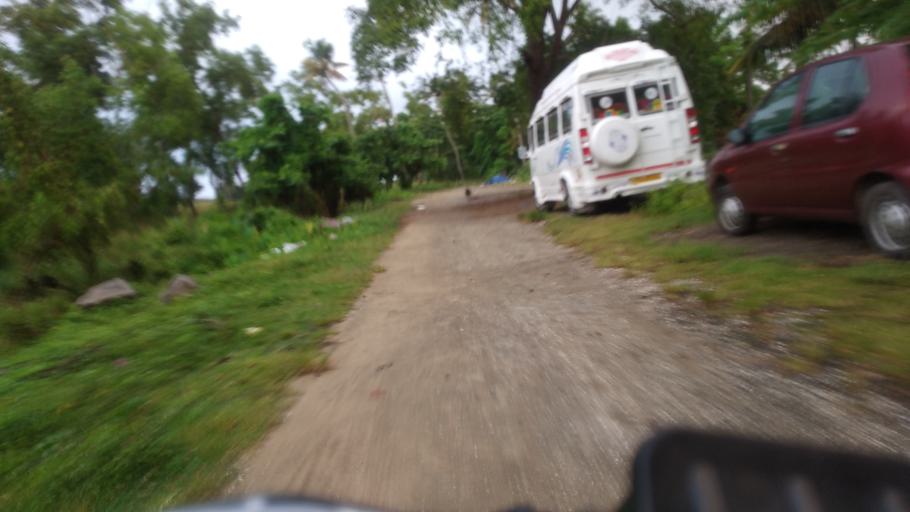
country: IN
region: Kerala
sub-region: Ernakulam
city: Cochin
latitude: 10.0105
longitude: 76.2172
